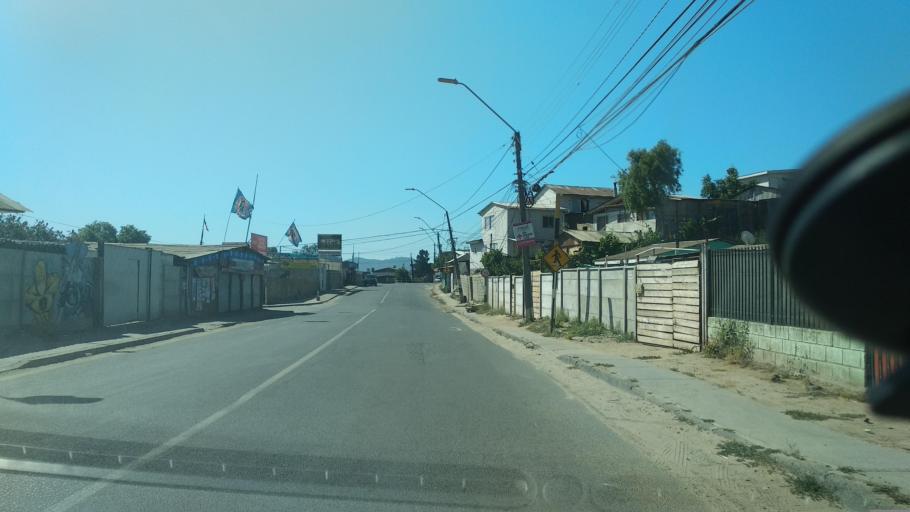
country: CL
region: Valparaiso
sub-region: Provincia de Marga Marga
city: Villa Alemana
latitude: -33.0612
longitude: -71.3714
